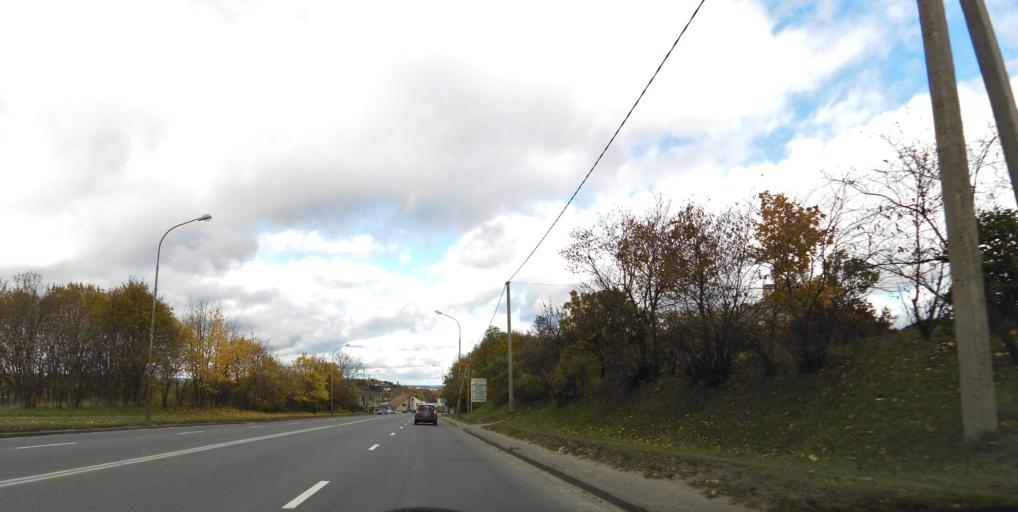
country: LT
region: Vilnius County
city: Rasos
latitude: 54.6583
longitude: 25.3035
